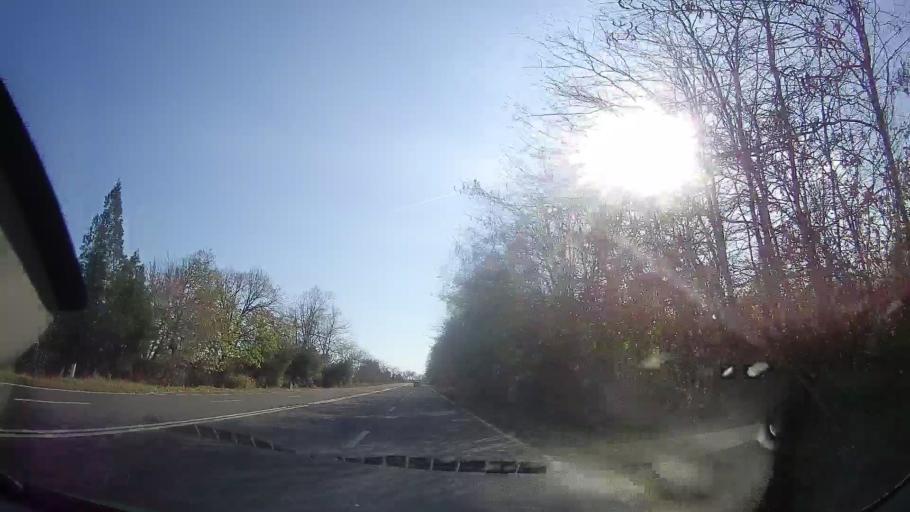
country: RO
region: Constanta
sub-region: Comuna Douazeci si Trei August
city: Douazeci si Trei August
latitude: 43.8897
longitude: 28.5726
